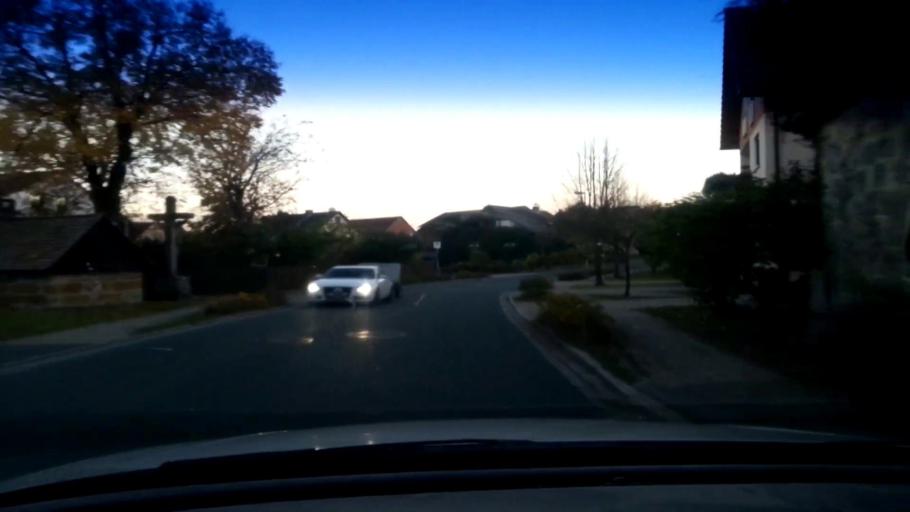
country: DE
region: Bavaria
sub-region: Upper Franconia
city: Poxdorf
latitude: 49.8737
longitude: 11.0925
